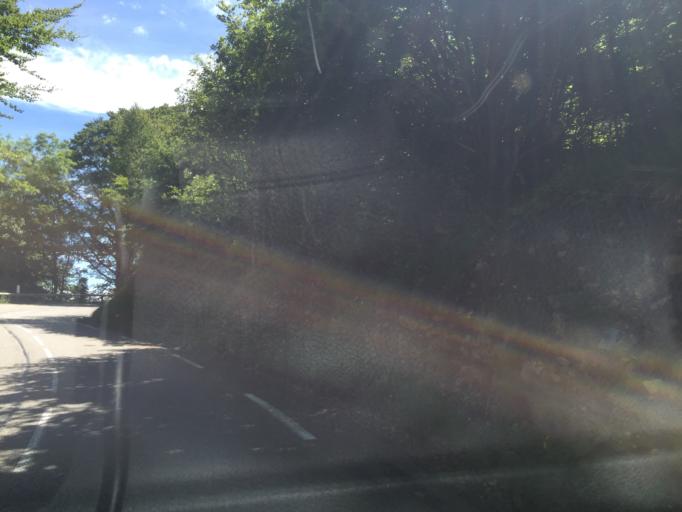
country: FR
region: Rhone-Alpes
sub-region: Departement de la Savoie
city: Saint-Baldoph
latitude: 45.4999
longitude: 5.9197
